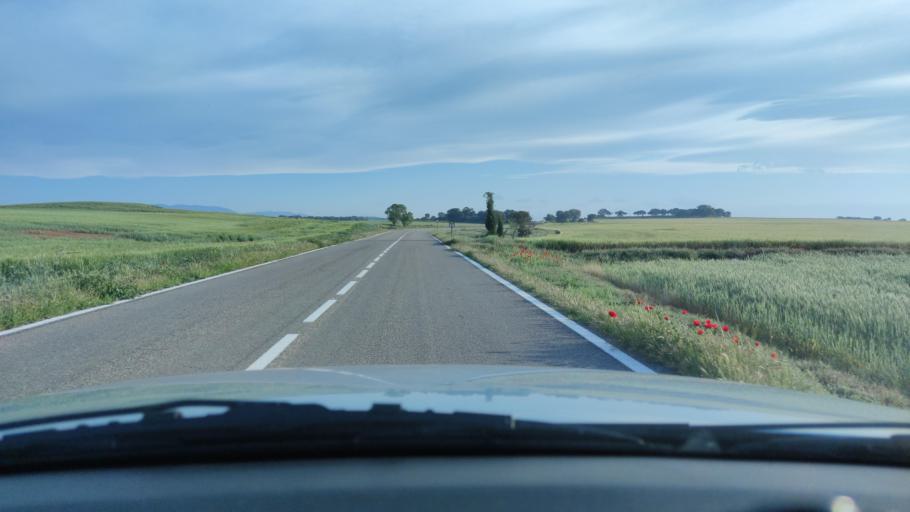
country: ES
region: Catalonia
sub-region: Provincia de Lleida
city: Agramunt
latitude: 41.8105
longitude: 1.0529
